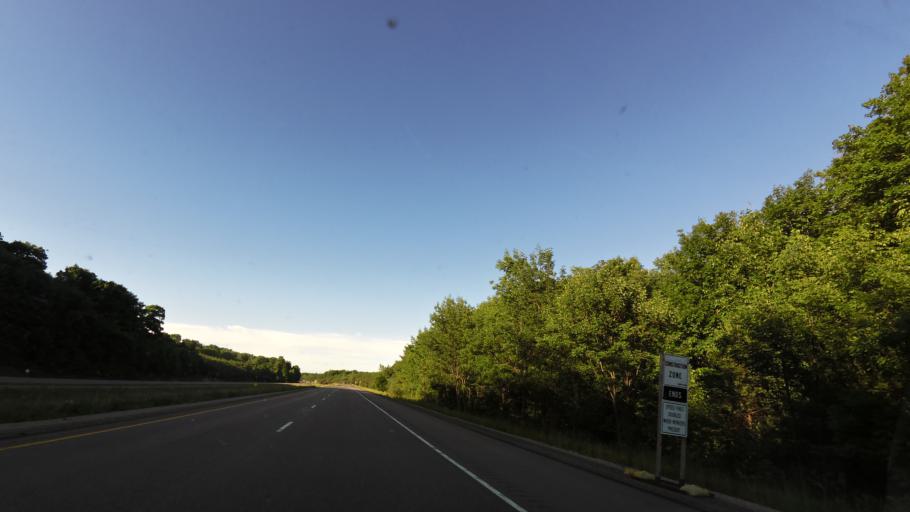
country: CA
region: Ontario
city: Barrie
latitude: 44.5929
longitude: -79.6821
